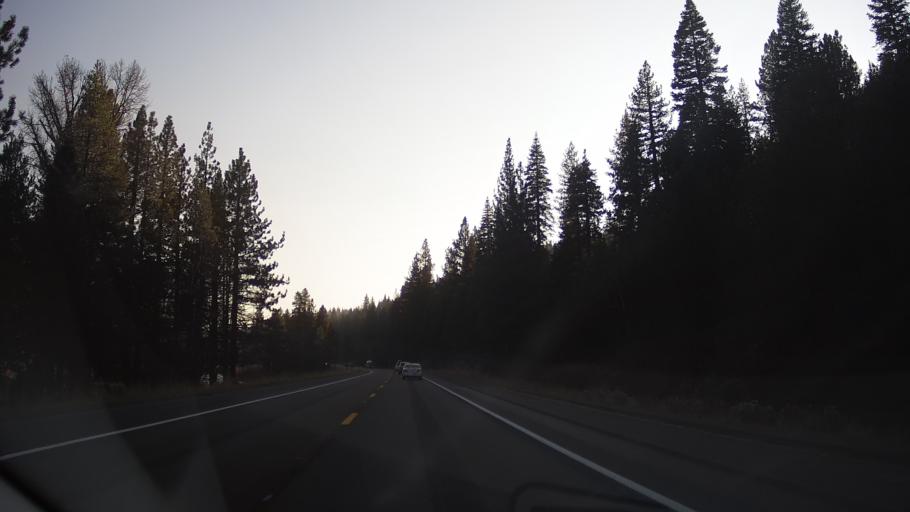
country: US
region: California
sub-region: Nevada County
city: Truckee
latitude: 39.2938
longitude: -120.2073
